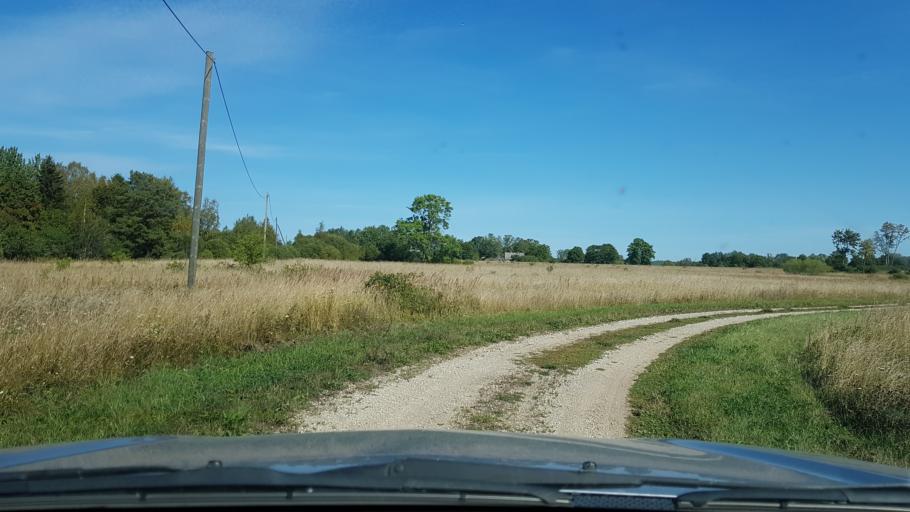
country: EE
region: Ida-Virumaa
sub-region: Sillamaee linn
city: Sillamae
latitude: 59.3808
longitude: 27.8081
